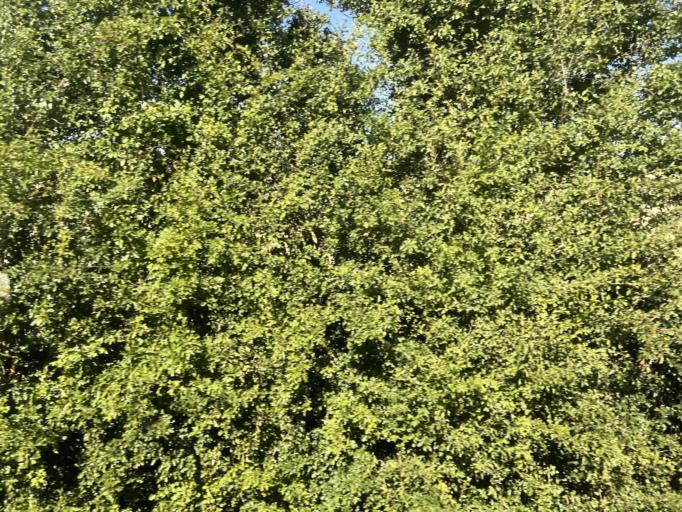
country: GB
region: England
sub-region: Lincolnshire
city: Spilsby
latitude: 53.0680
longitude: 0.0688
